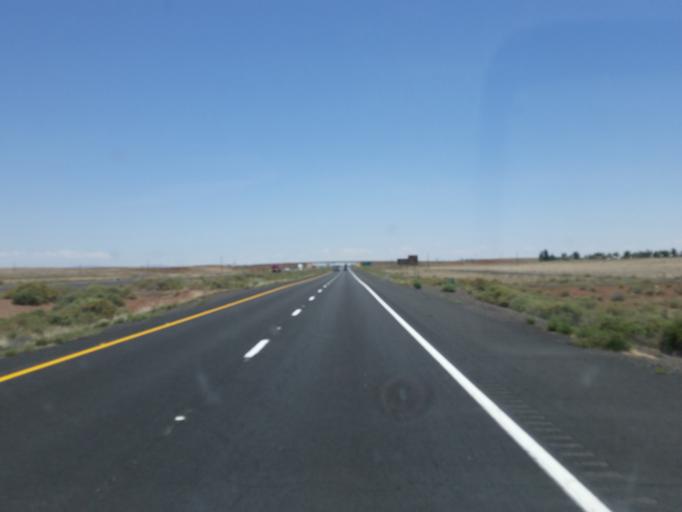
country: US
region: Arizona
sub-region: Coconino County
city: LeChee
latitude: 35.1113
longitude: -111.0424
